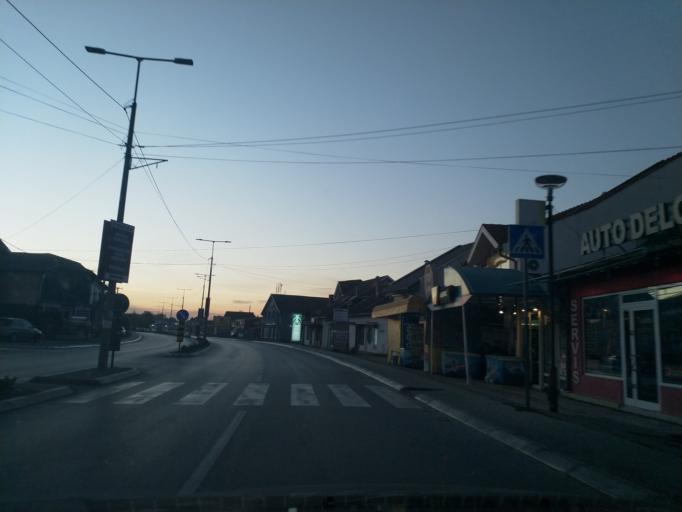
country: RS
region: Central Serbia
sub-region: Pomoravski Okrug
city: Svilajnac
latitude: 44.2325
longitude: 21.1904
